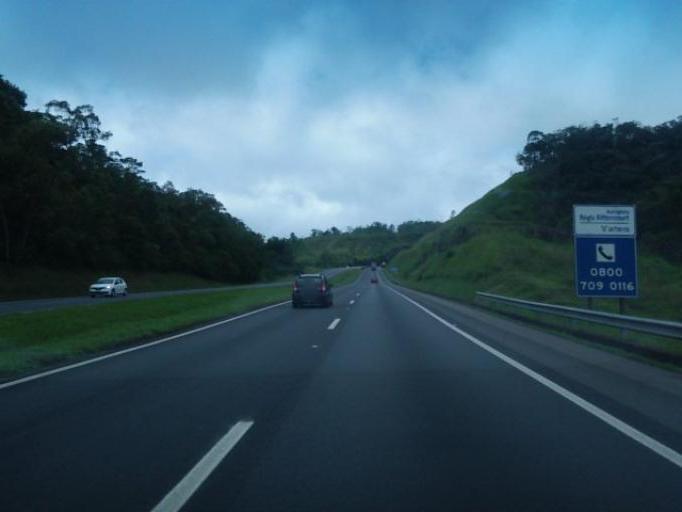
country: BR
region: Parana
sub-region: Antonina
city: Antonina
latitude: -25.1022
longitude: -48.7345
